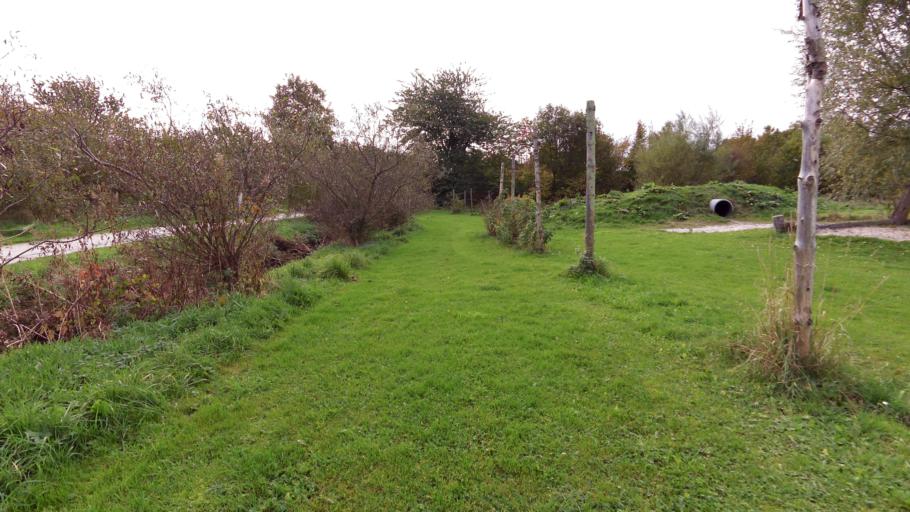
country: DK
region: Central Jutland
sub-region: Arhus Kommune
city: Stavtrup
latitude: 56.1182
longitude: 10.1303
